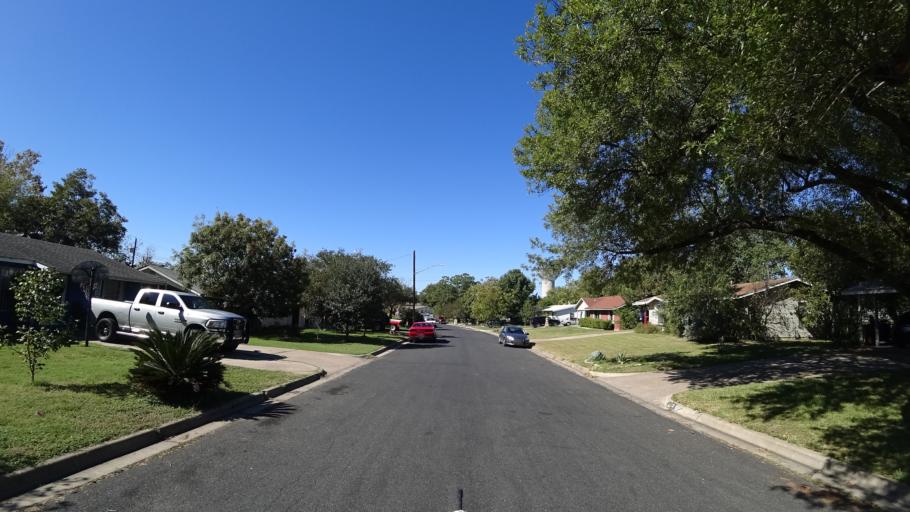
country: US
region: Texas
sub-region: Travis County
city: Austin
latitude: 30.3007
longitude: -97.6884
